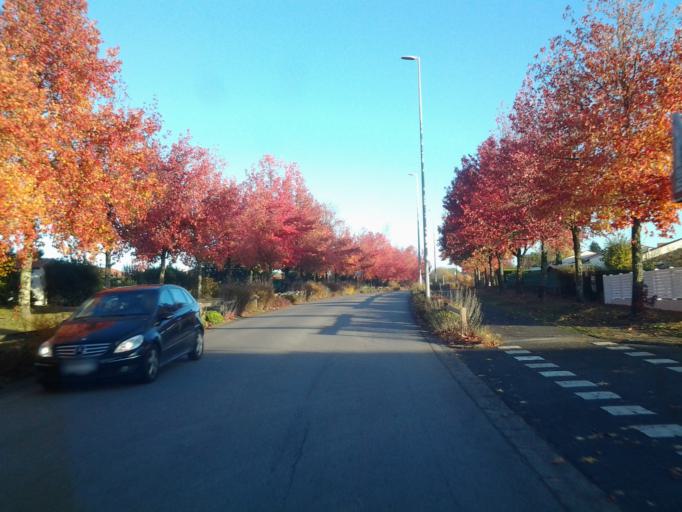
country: FR
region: Pays de la Loire
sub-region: Departement de la Vendee
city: La Roche-sur-Yon
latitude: 46.6621
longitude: -1.4117
